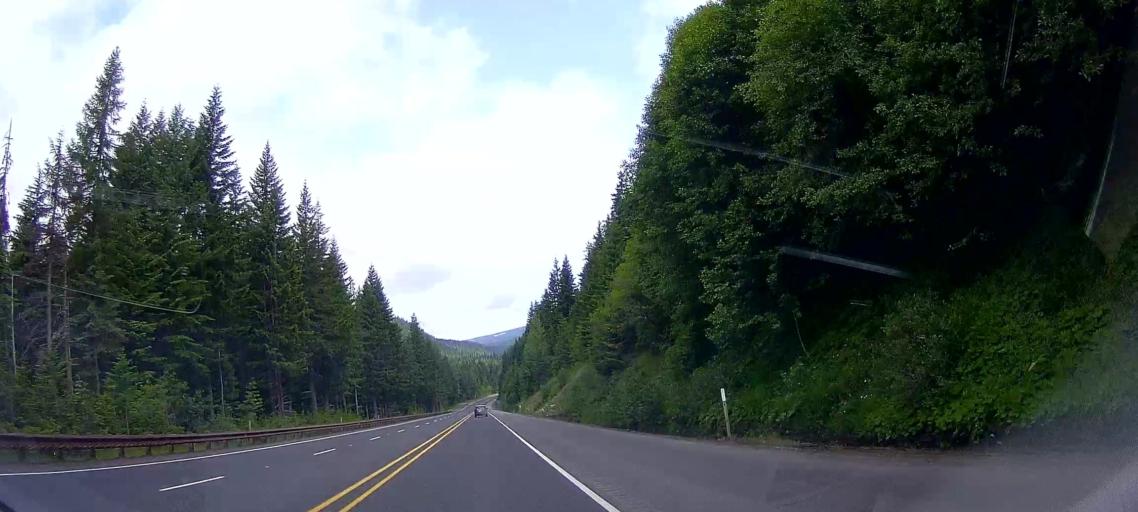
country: US
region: Oregon
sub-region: Clackamas County
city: Mount Hood Village
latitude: 45.2445
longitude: -121.7076
